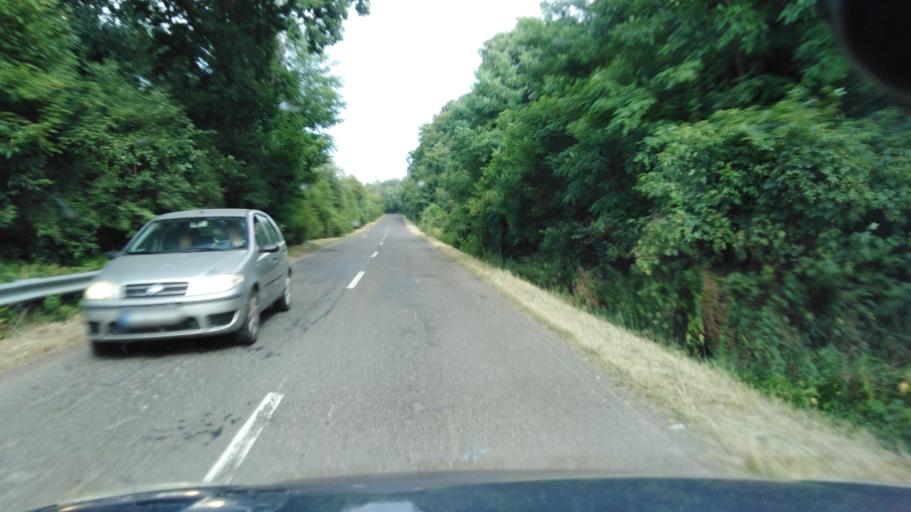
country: HU
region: Nograd
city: Karancskeszi
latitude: 48.2084
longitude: 19.5798
